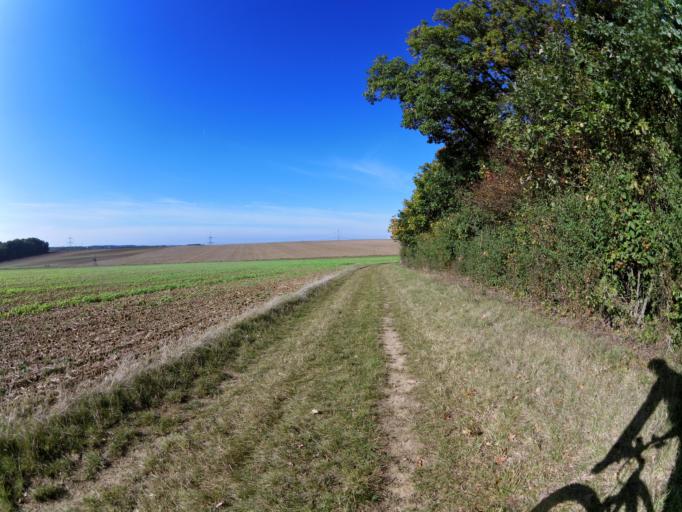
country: DE
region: Bavaria
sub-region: Regierungsbezirk Unterfranken
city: Ochsenfurt
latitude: 49.6787
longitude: 10.0634
